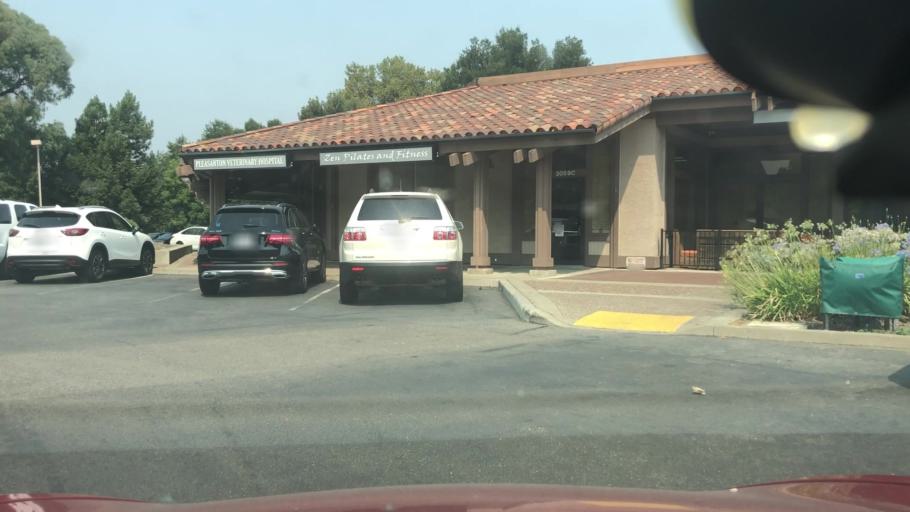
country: US
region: California
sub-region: Alameda County
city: Pleasanton
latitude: 37.6773
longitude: -121.8962
